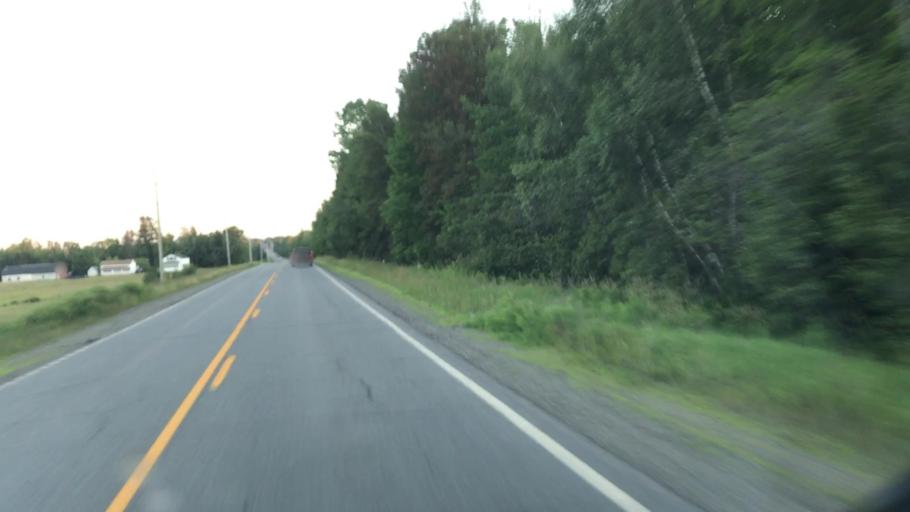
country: US
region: Maine
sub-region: Penobscot County
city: Medway
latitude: 45.6135
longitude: -68.3043
